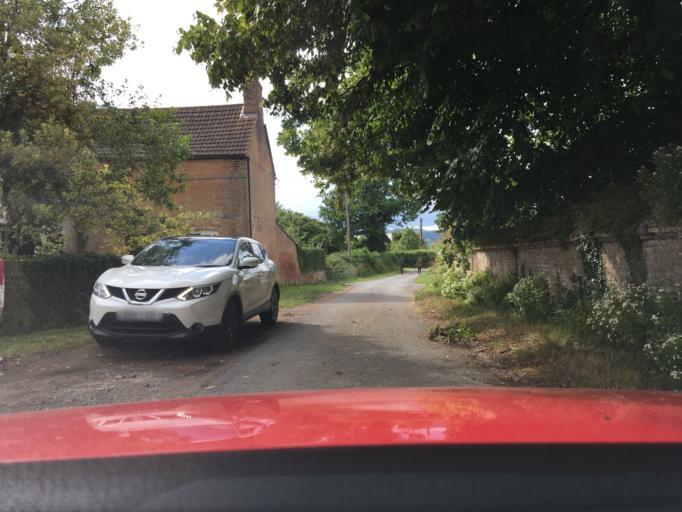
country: GB
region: England
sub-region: Gloucestershire
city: Cinderford
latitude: 51.8001
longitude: -2.4167
